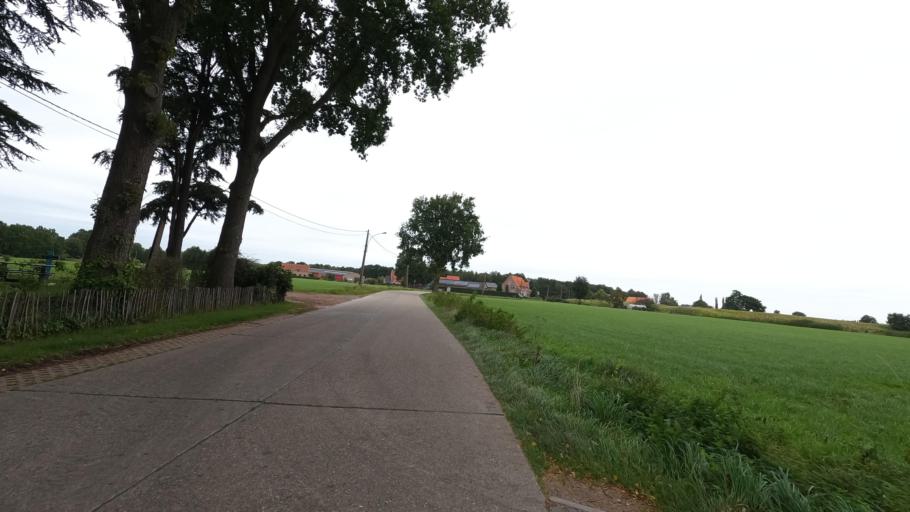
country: BE
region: Flanders
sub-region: Provincie Antwerpen
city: Rijkevorsel
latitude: 51.3514
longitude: 4.7726
